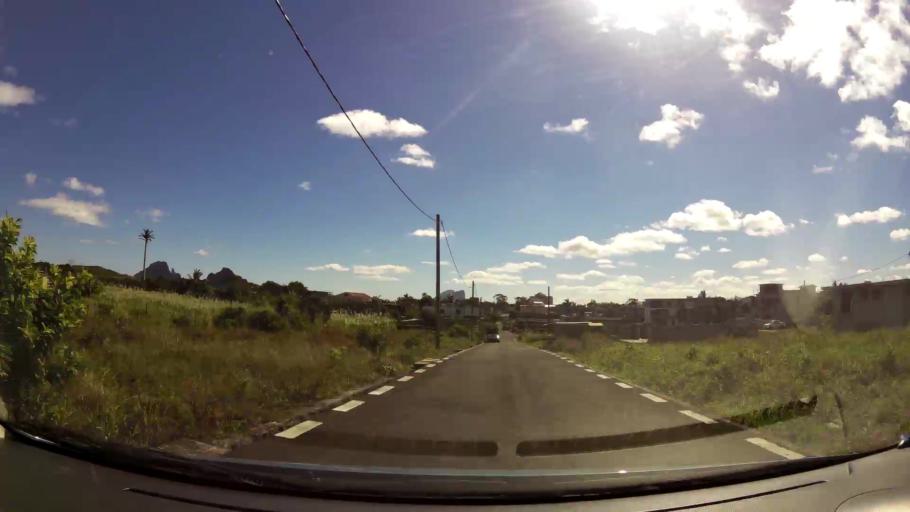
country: MU
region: Plaines Wilhems
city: Vacoas
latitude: -20.3359
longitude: 57.4780
